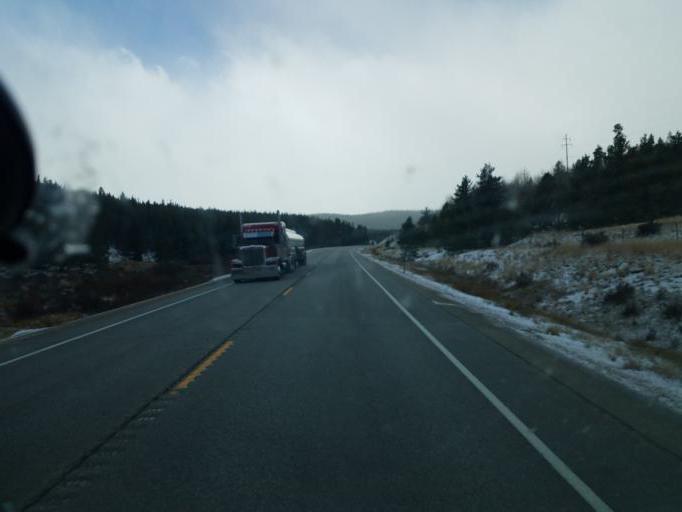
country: US
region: Colorado
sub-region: Clear Creek County
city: Georgetown
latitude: 39.4375
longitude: -105.7530
